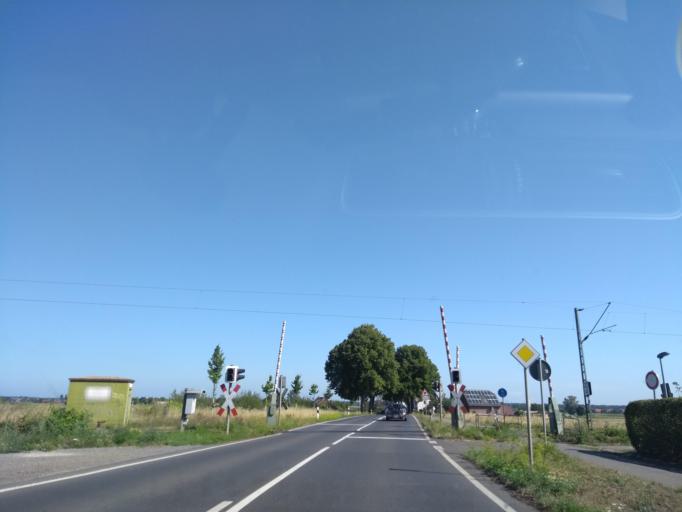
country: DE
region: Lower Saxony
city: Bad Nenndorf
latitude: 52.3408
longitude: 9.3891
